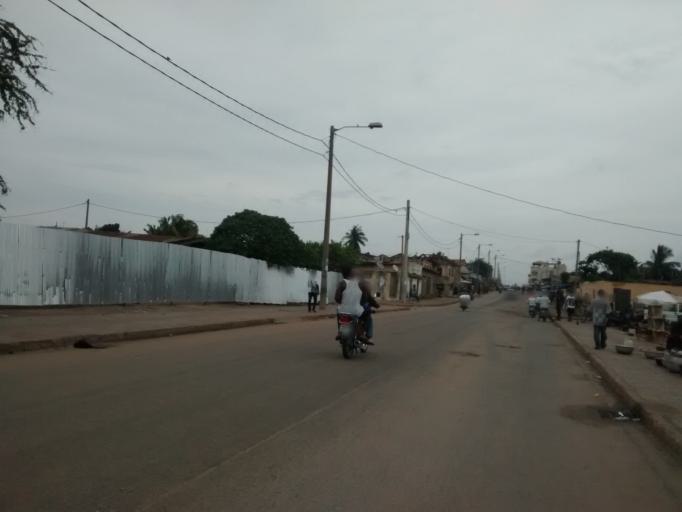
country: TG
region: Maritime
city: Lome
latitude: 6.1418
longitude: 1.2174
